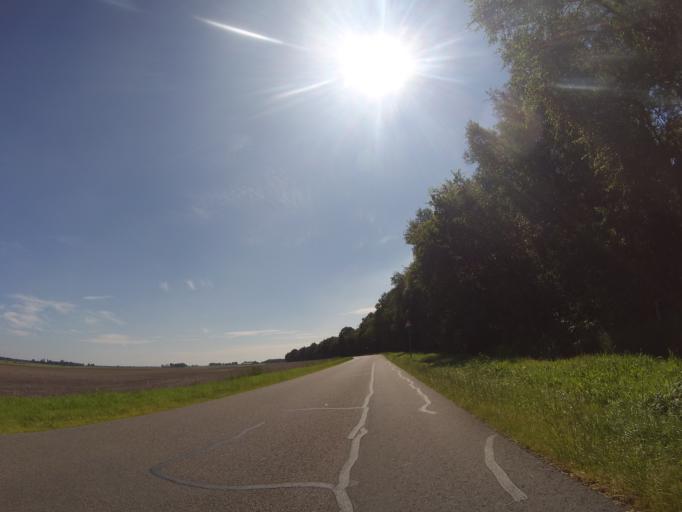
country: NL
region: Drenthe
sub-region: Gemeente Emmen
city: Klazienaveen
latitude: 52.6900
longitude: 6.9536
